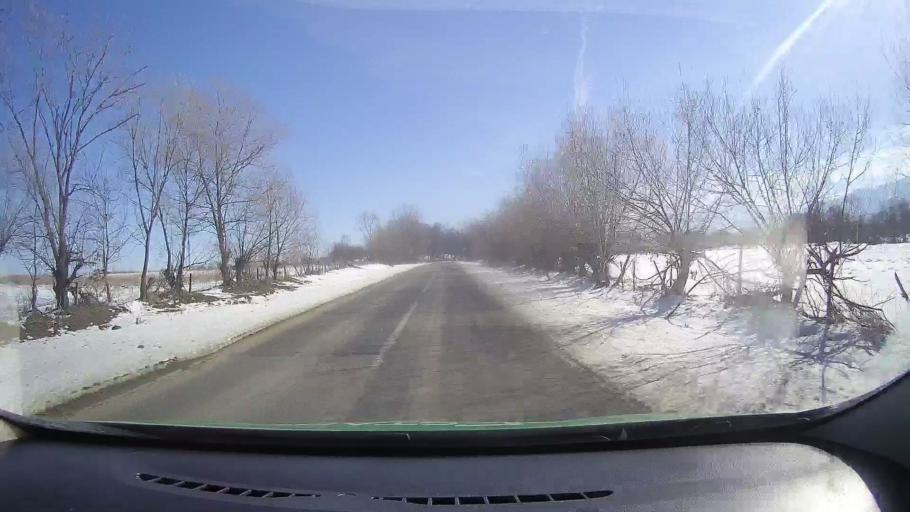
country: RO
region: Brasov
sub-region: Comuna Harseni
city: Harseni
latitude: 45.7344
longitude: 25.0039
